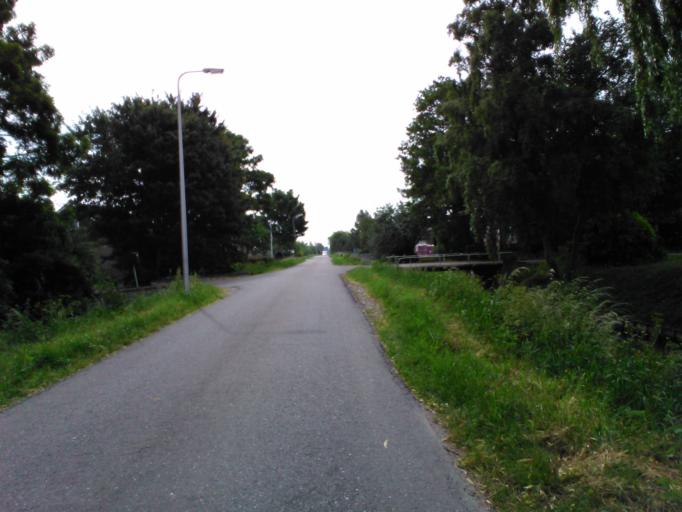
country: NL
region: South Holland
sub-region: Gemeente Waddinxveen
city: Waddinxveen
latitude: 51.9935
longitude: 4.6098
